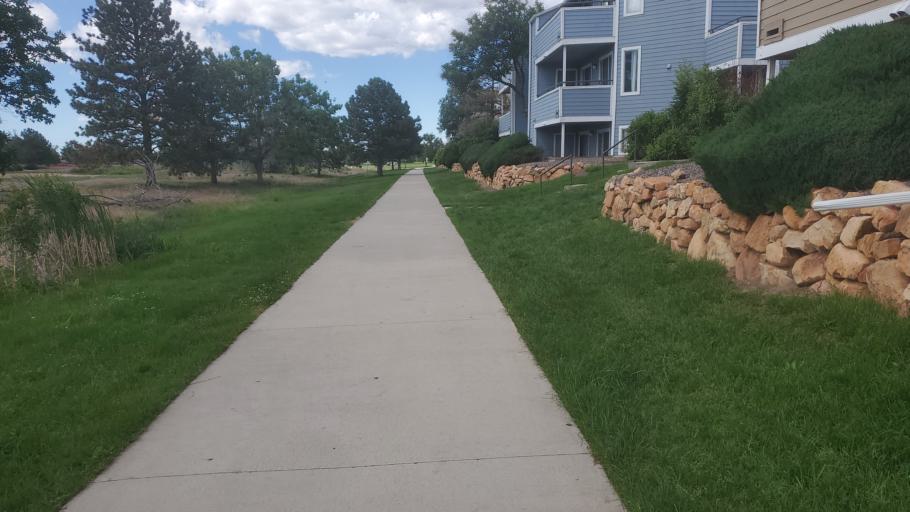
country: US
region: Colorado
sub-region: Adams County
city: Aurora
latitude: 39.6765
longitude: -104.8443
